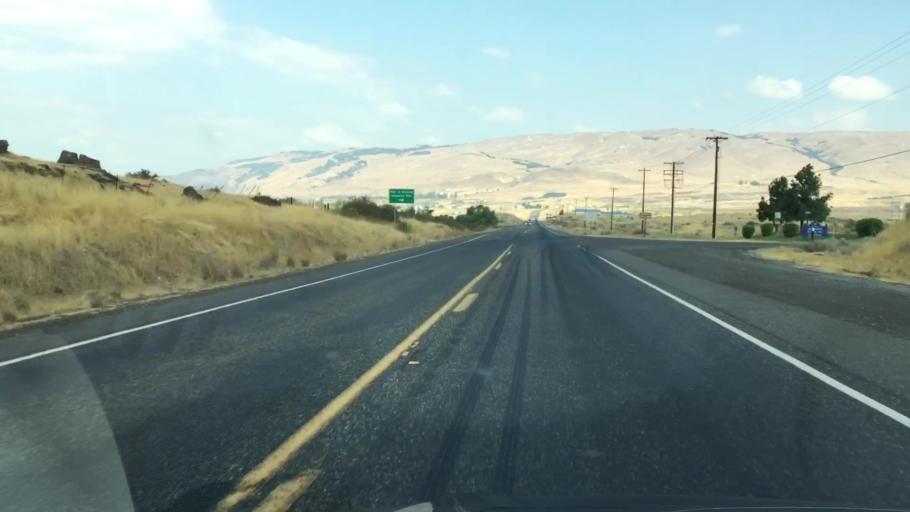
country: US
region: Washington
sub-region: Klickitat County
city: Dallesport
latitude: 45.6209
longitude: -121.1460
